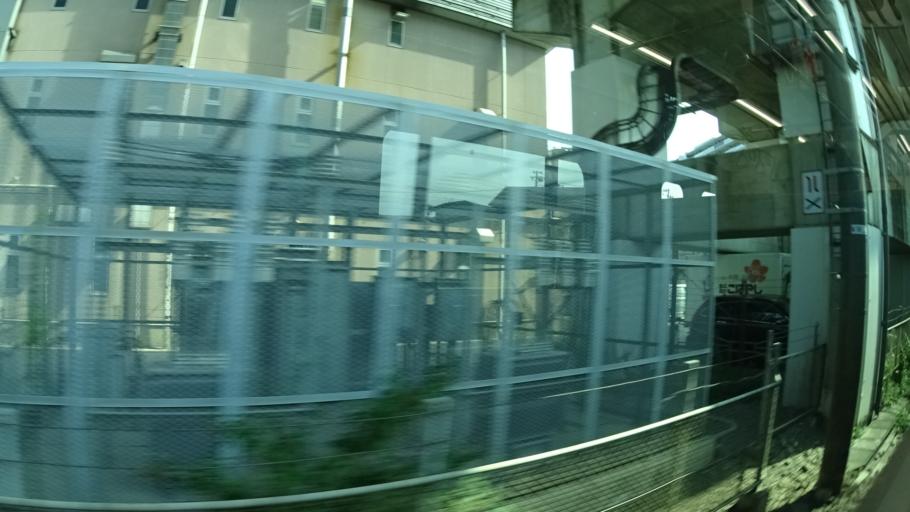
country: JP
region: Miyagi
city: Sendai-shi
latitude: 38.2688
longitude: 140.8942
